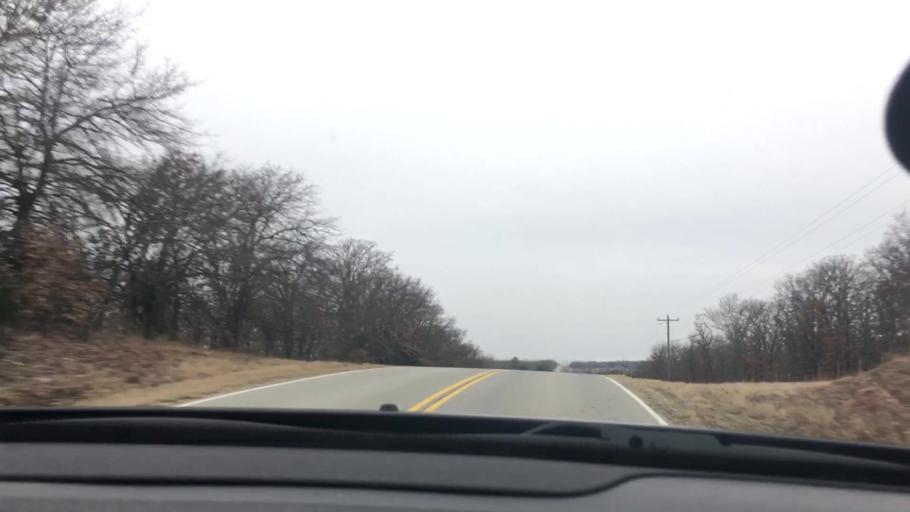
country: US
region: Oklahoma
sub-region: Coal County
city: Coalgate
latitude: 34.5056
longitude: -96.3174
